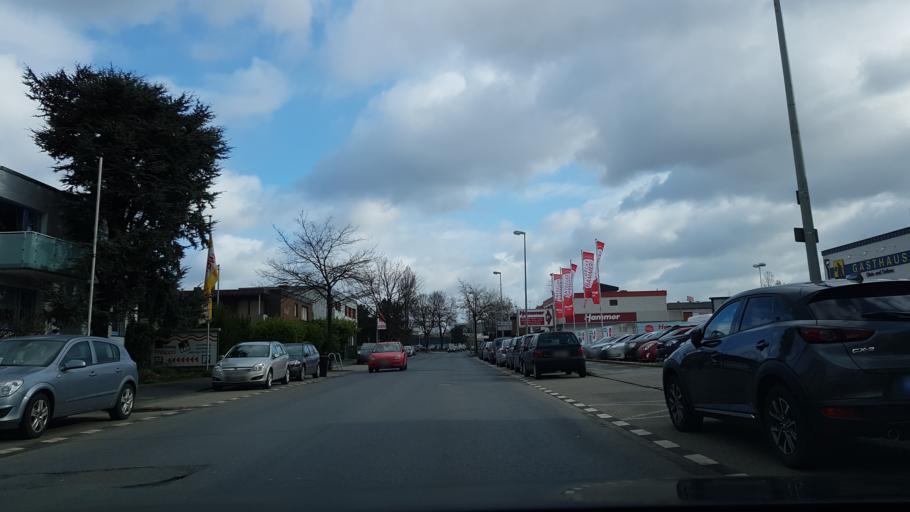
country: DE
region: North Rhine-Westphalia
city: Meiderich
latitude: 51.4883
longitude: 6.8008
